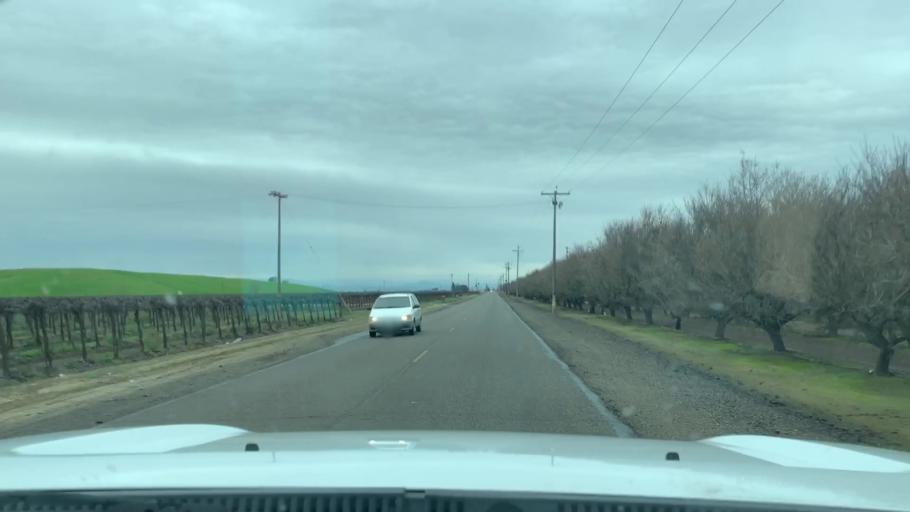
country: US
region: California
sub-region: Fresno County
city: Caruthers
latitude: 36.5473
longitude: -119.7488
